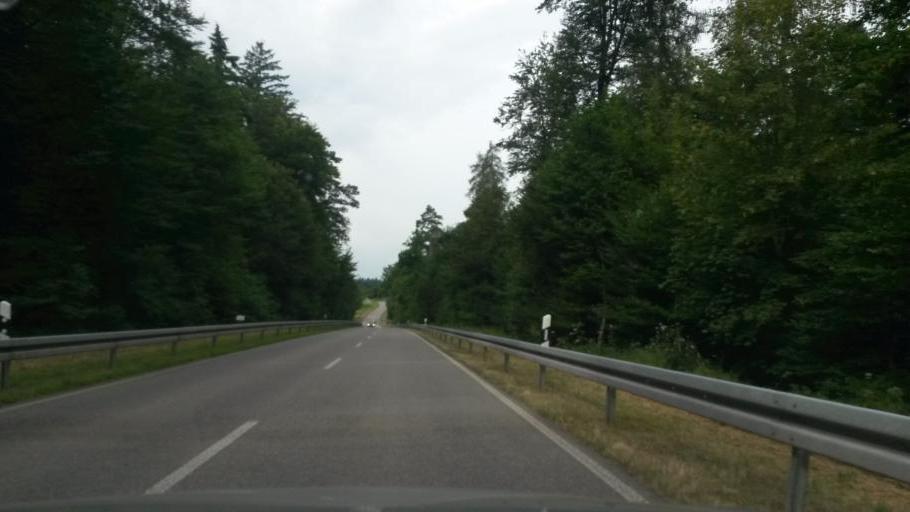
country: DE
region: Baden-Wuerttemberg
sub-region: Karlsruhe Region
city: Konigsbach-Stein
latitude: 48.9245
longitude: 8.5192
